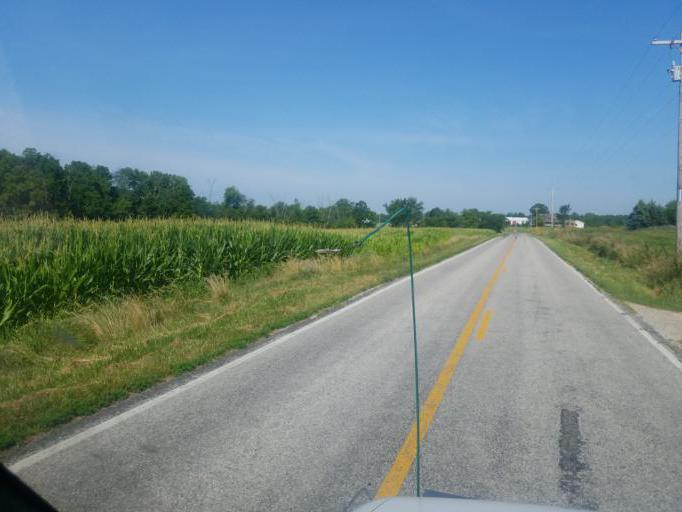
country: US
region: Ohio
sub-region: Union County
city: New California
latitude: 40.2825
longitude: -83.2295
